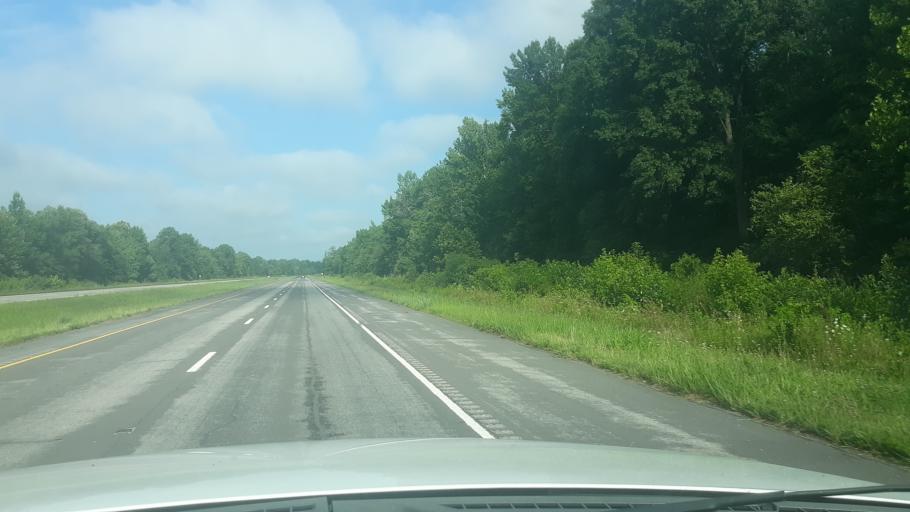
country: US
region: Illinois
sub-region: Saline County
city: Carrier Mills
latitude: 37.7343
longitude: -88.6866
